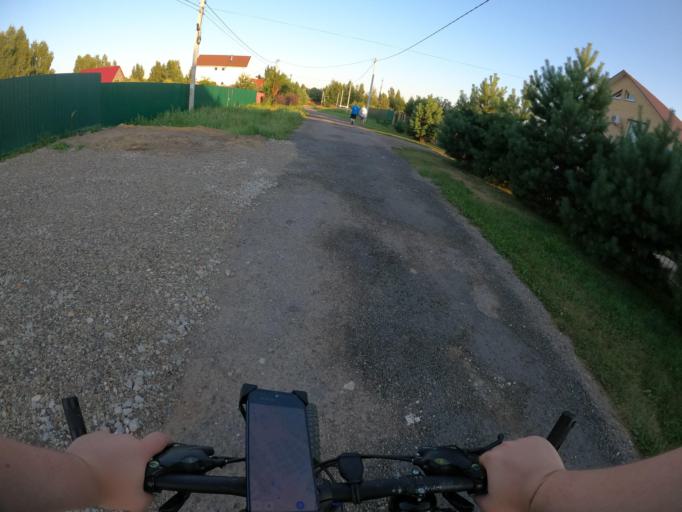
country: RU
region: Moskovskaya
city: Beloozerskiy
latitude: 55.4617
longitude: 38.4248
